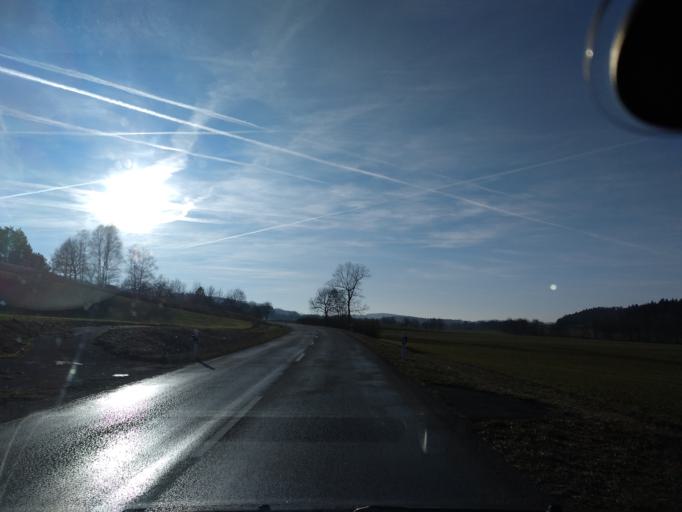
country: DE
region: Baden-Wuerttemberg
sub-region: Regierungsbezirk Stuttgart
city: Crailsheim
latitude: 49.0917
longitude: 10.0388
